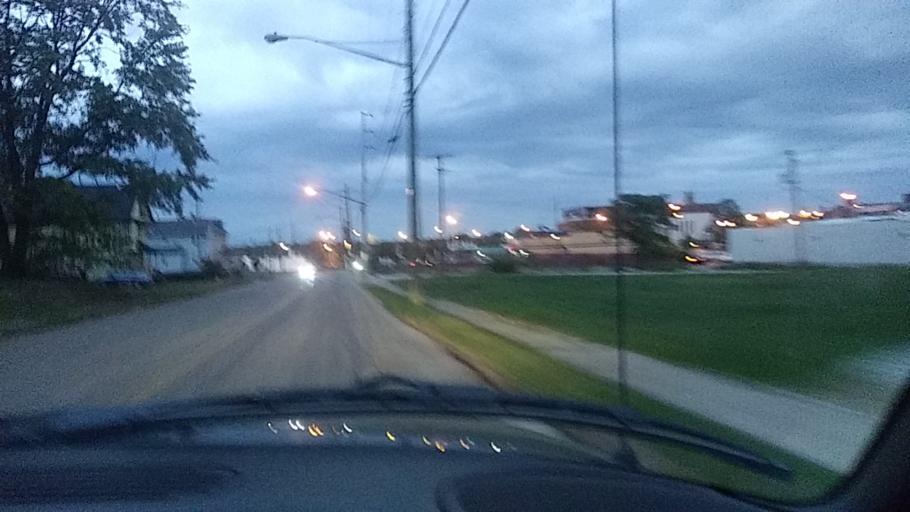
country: US
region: Ohio
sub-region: Summit County
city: Akron
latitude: 41.0575
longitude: -81.5312
